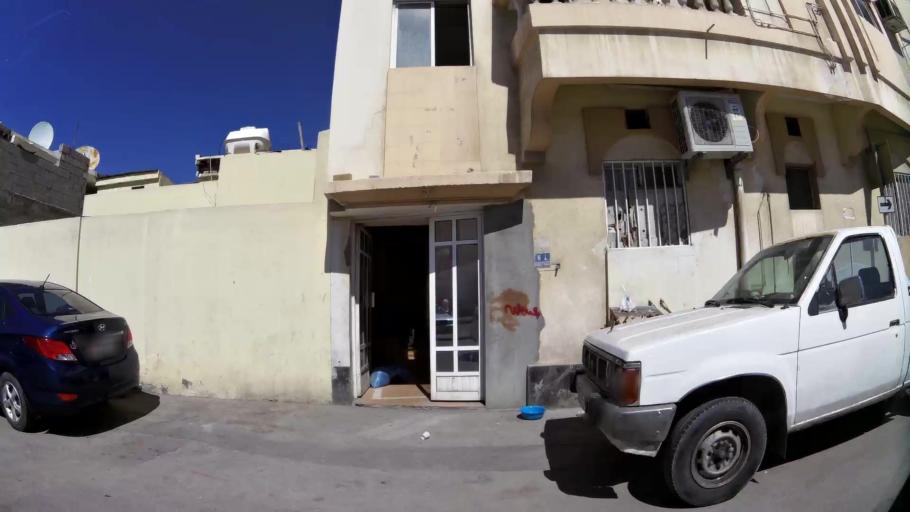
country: BH
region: Muharraq
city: Al Muharraq
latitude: 26.2460
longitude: 50.6175
